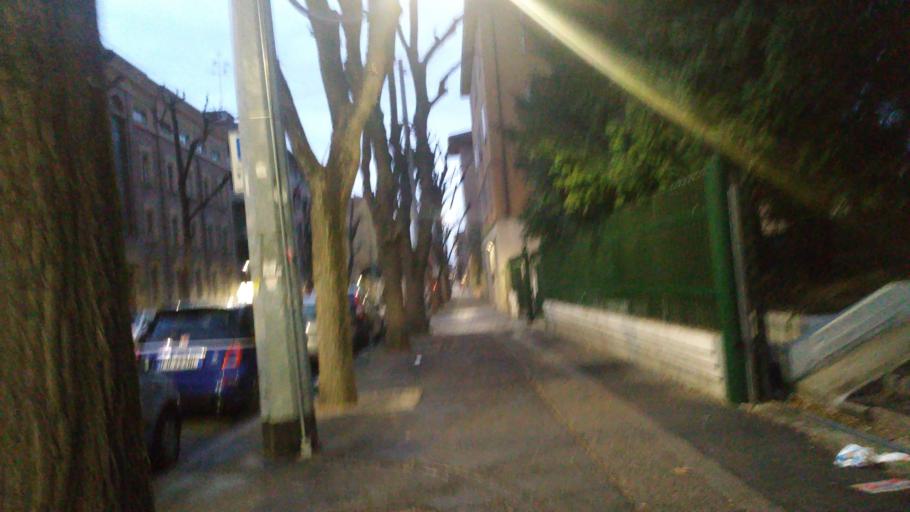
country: IT
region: Emilia-Romagna
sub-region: Provincia di Bologna
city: Bologna
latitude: 44.5009
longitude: 11.3273
